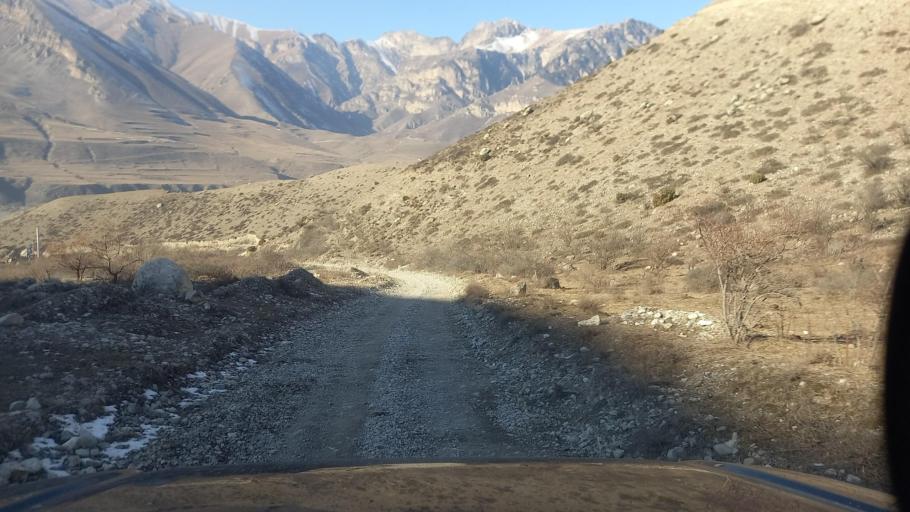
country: RU
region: Ingushetiya
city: Dzhayrakh
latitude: 42.8452
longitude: 44.6569
